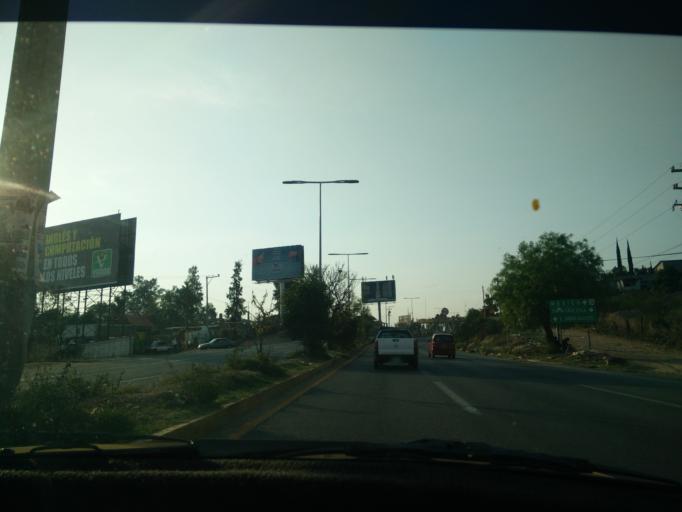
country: MX
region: Oaxaca
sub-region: Santa Maria Atzompa
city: Fraccionamiento Riberas de San Jeronimo
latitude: 17.1343
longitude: -96.7738
